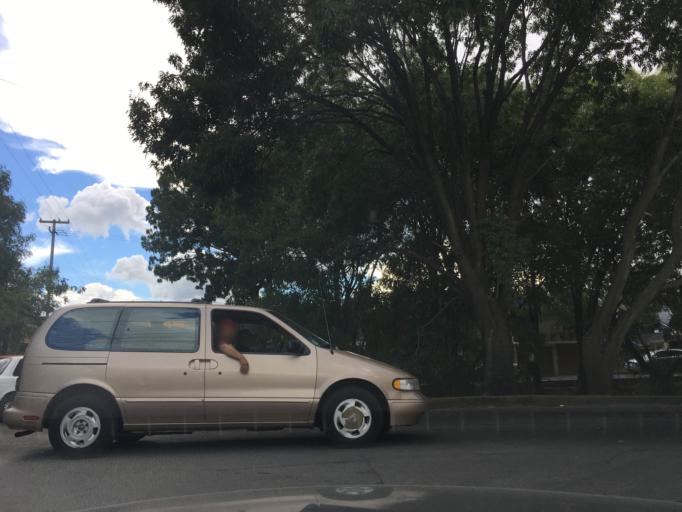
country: MX
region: Michoacan
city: Morelia
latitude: 19.6917
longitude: -101.1927
